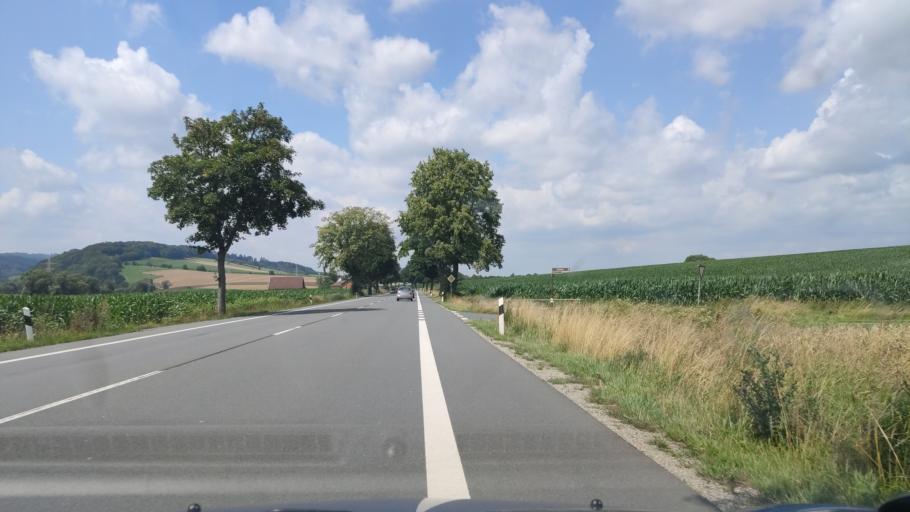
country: DE
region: Lower Saxony
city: Luerdissen
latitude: 51.9513
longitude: 9.6179
